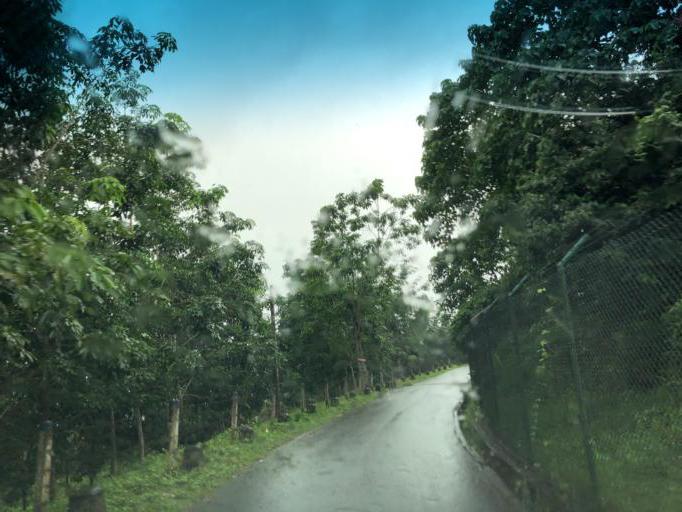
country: LK
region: Western
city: Horana South
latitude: 6.7209
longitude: 80.0614
